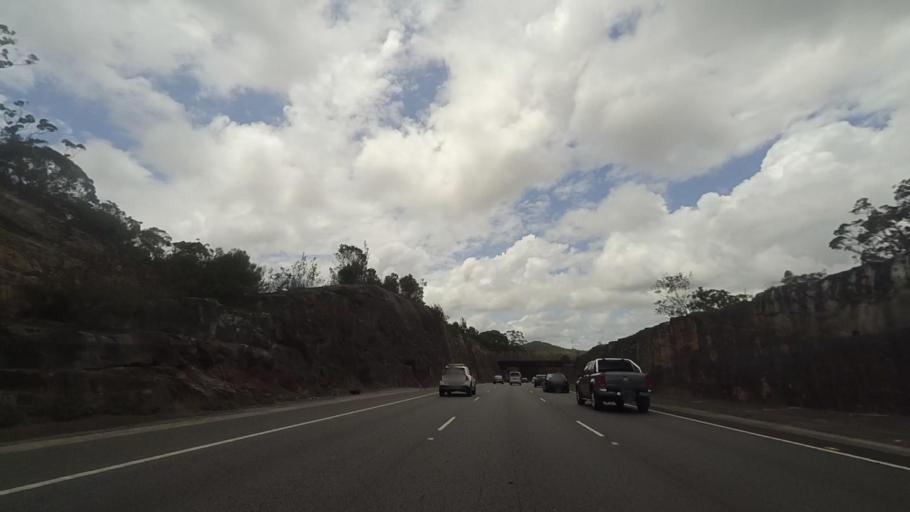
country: AU
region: New South Wales
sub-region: Gosford Shire
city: Umina
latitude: -33.4656
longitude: 151.1944
